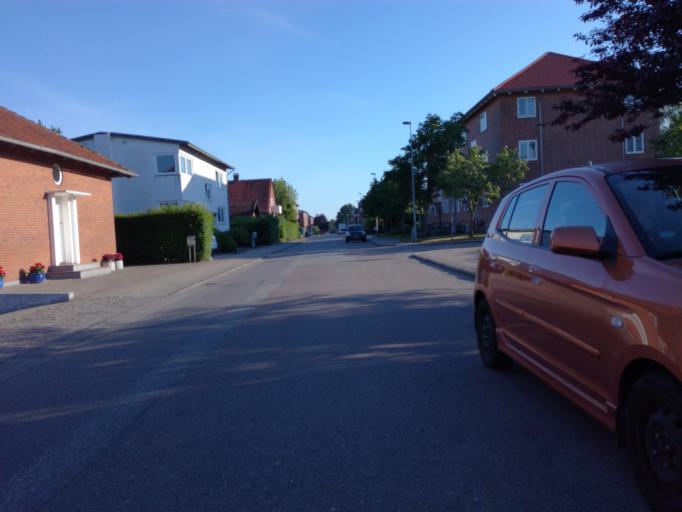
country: DK
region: South Denmark
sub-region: Fredericia Kommune
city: Fredericia
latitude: 55.5736
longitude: 9.7637
